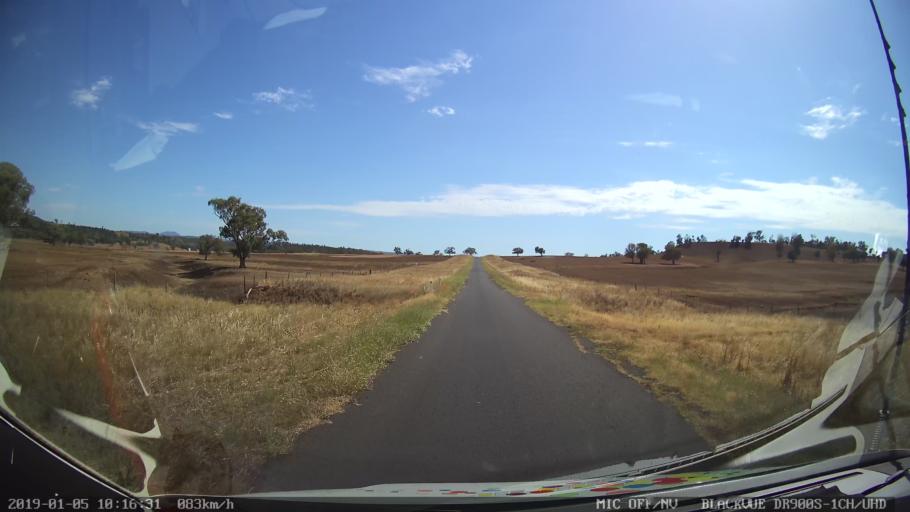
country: AU
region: New South Wales
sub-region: Gilgandra
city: Gilgandra
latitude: -31.5744
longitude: 148.9531
